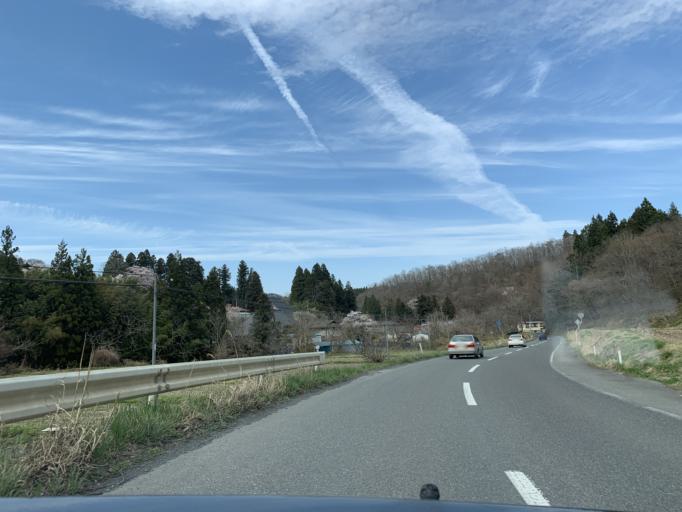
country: JP
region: Iwate
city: Ichinoseki
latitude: 38.8410
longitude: 141.3405
